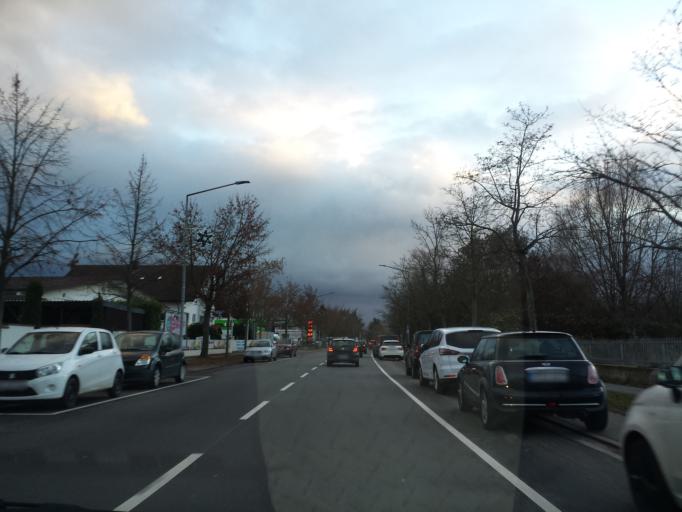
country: DE
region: Hesse
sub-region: Regierungsbezirk Darmstadt
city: Bensheim
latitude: 49.7007
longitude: 8.6102
